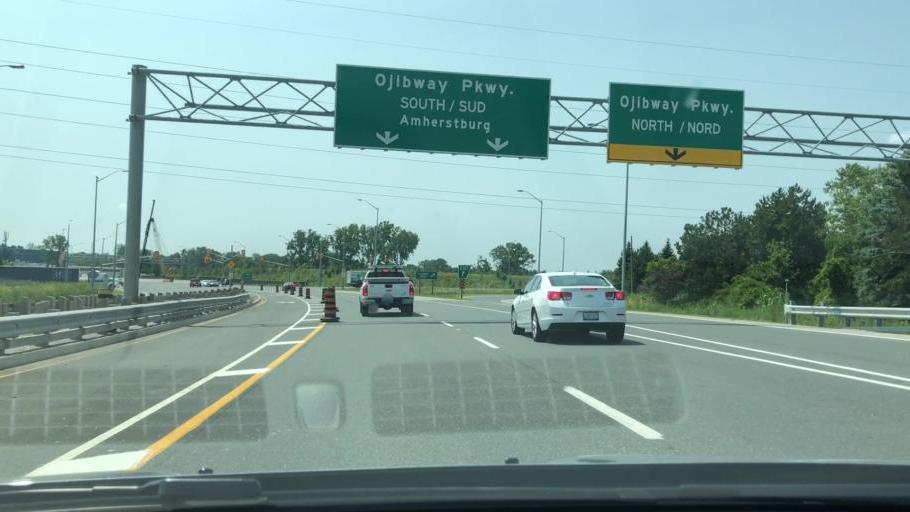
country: US
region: Michigan
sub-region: Wayne County
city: River Rouge
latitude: 42.2750
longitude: -83.0771
